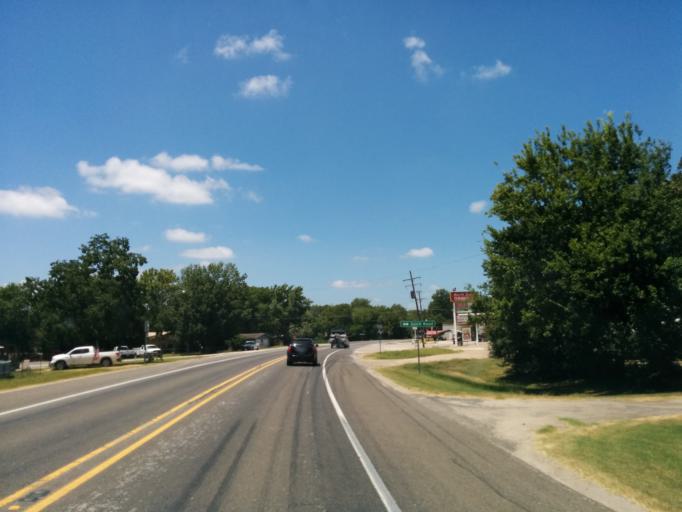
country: US
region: Texas
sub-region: Leon County
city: Hilltop Lakes
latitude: 30.9149
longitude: -96.1057
